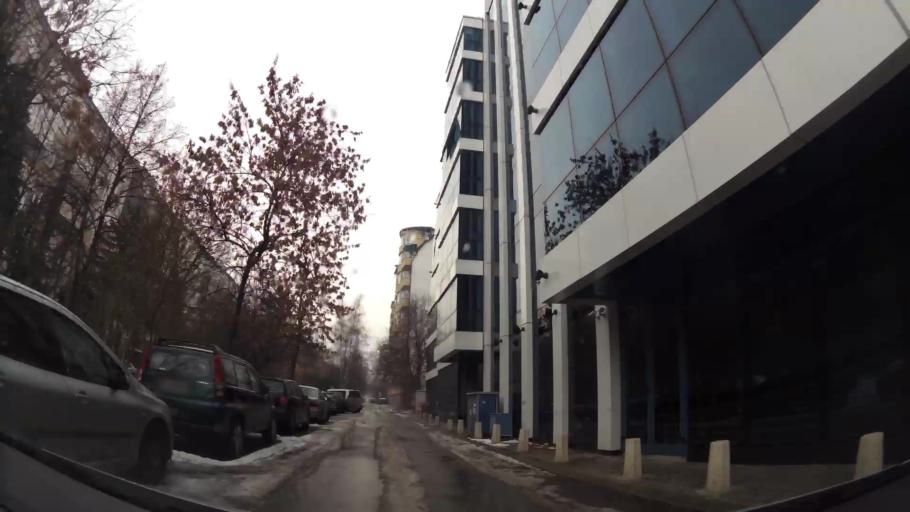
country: BG
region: Sofia-Capital
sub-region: Stolichna Obshtina
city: Sofia
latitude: 42.6734
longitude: 23.2770
